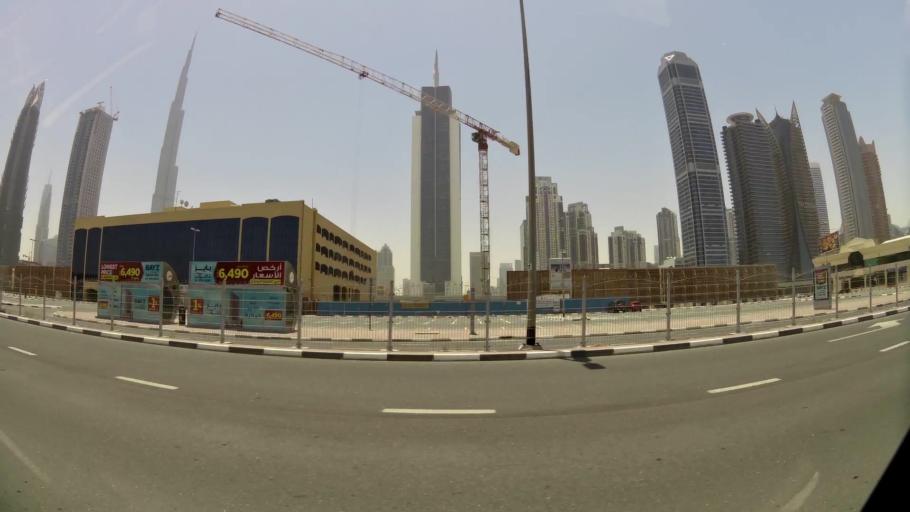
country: AE
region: Dubai
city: Dubai
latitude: 25.1972
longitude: 55.2624
